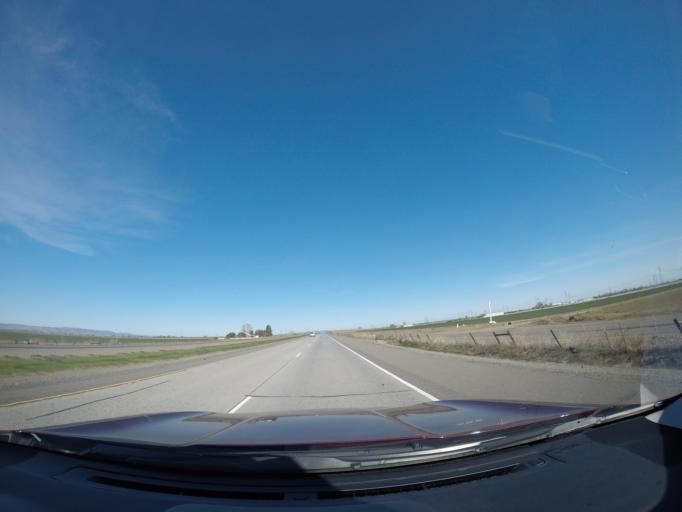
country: US
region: California
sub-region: Yolo County
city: Cottonwood
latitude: 38.6562
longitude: -121.9517
